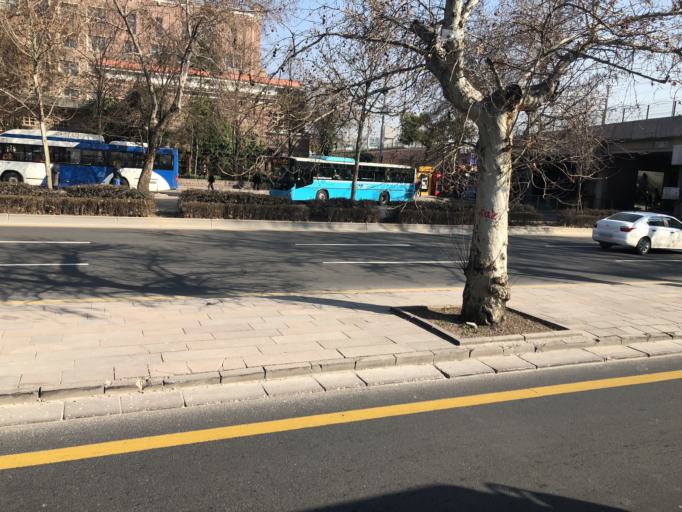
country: TR
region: Ankara
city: Ankara
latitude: 39.9295
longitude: 32.8545
